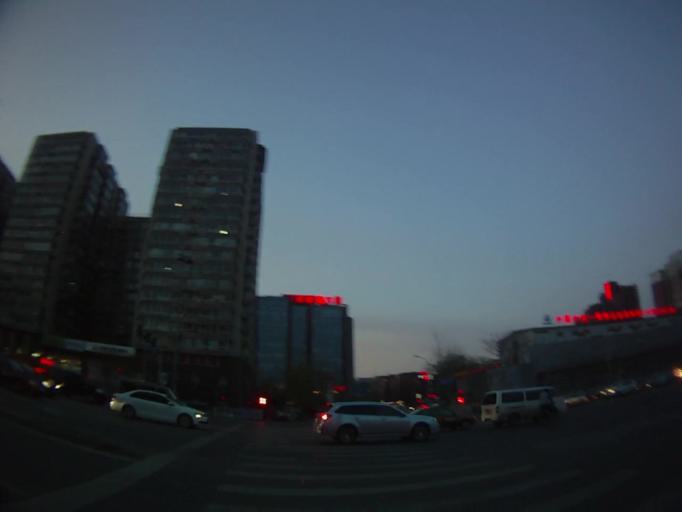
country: CN
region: Beijing
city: Longtan
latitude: 39.8920
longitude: 116.4326
